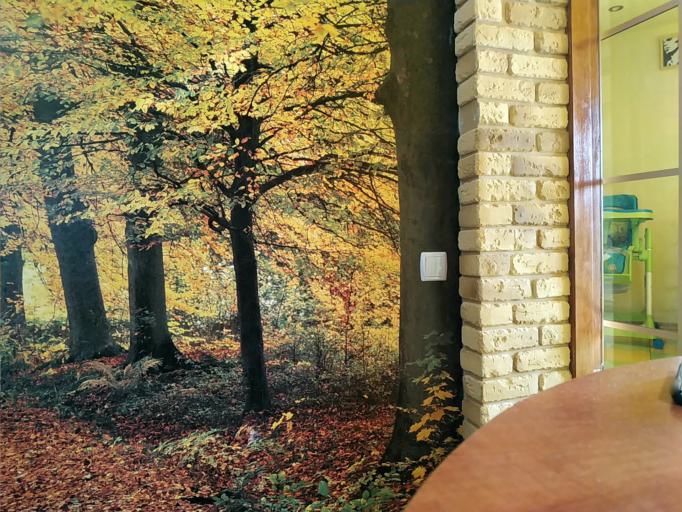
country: RU
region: Novgorod
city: Parfino
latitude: 57.7988
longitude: 31.6187
